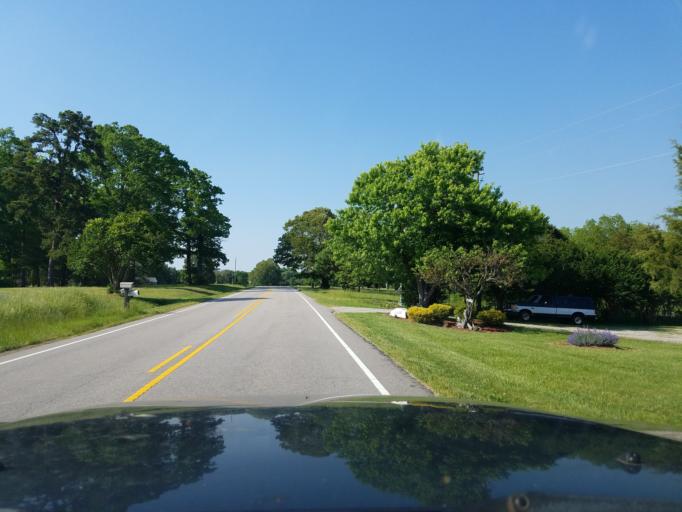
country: US
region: North Carolina
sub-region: Vance County
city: Henderson
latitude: 36.3774
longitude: -78.3699
